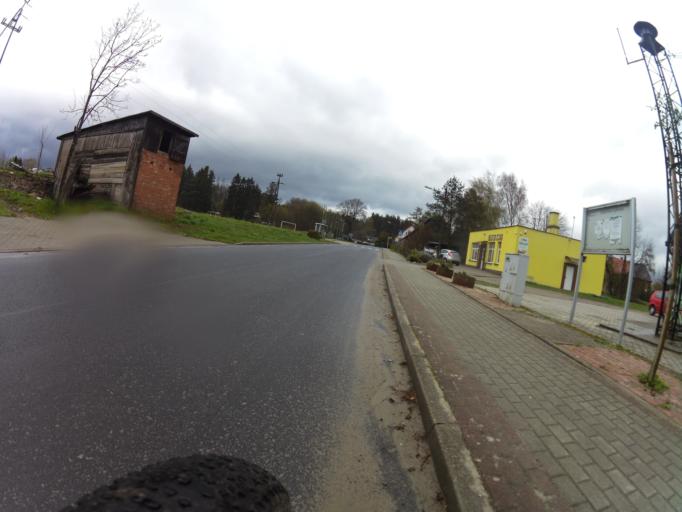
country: PL
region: Pomeranian Voivodeship
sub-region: Powiat slupski
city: Kepice
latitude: 54.2821
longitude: 16.8133
